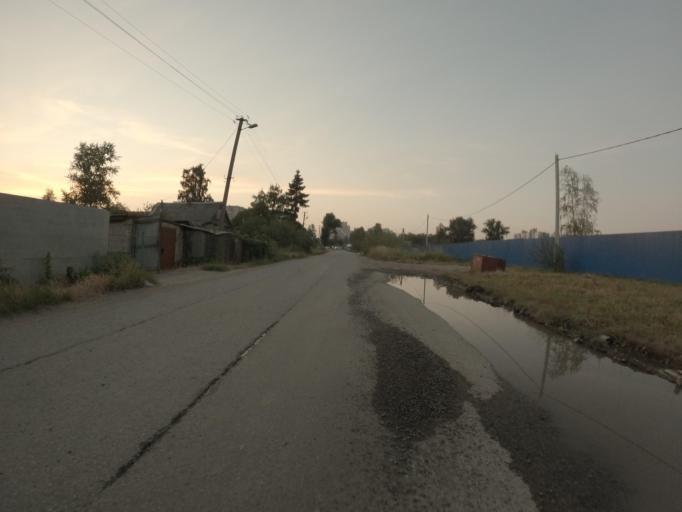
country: RU
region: Leningrad
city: Yanino Vtoroye
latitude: 59.9454
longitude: 30.5550
